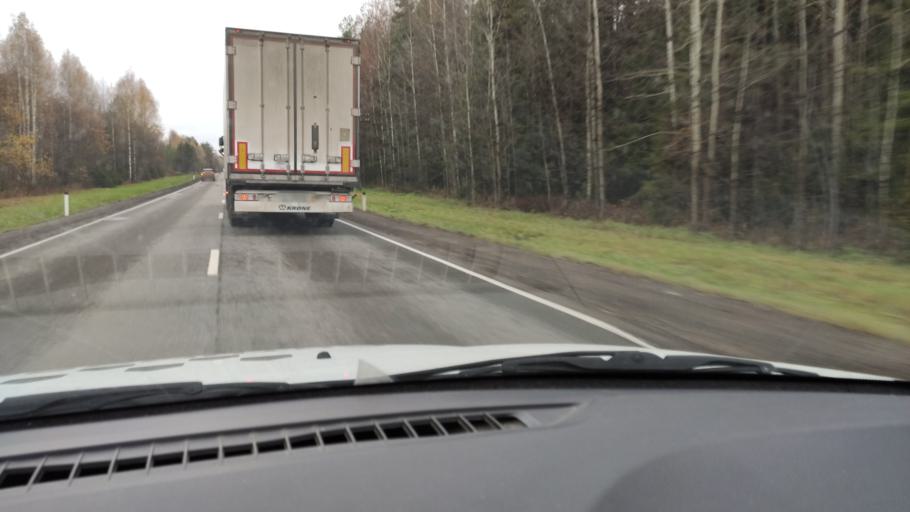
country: RU
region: Kirov
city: Belaya Kholunitsa
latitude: 58.7925
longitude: 50.5193
